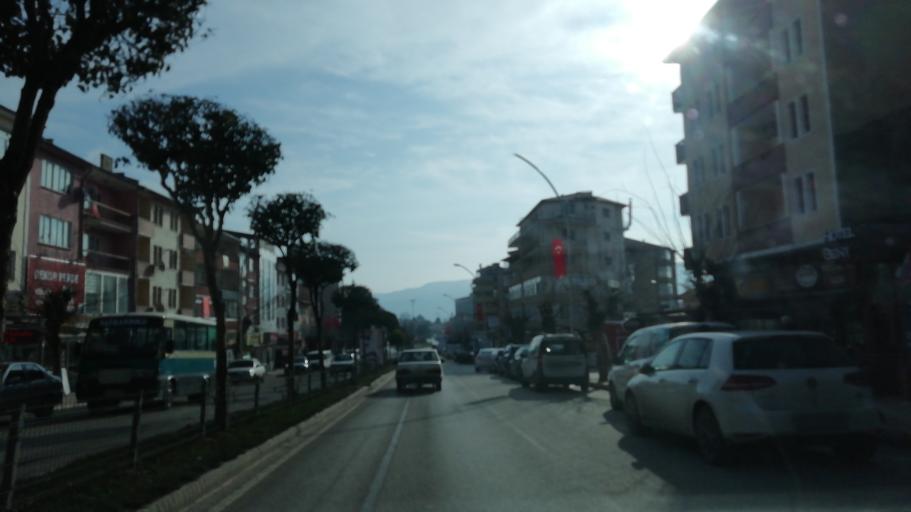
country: TR
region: Karabuk
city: Safranbolu
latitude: 41.2525
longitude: 32.6796
